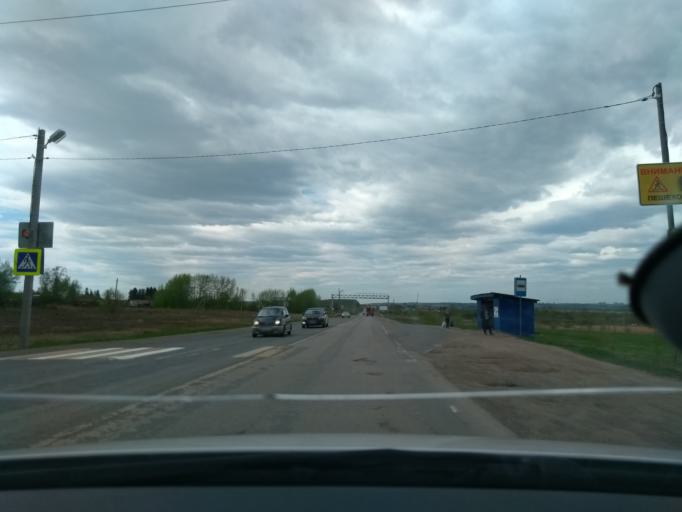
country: RU
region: Perm
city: Lobanovo
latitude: 57.8669
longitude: 56.2899
